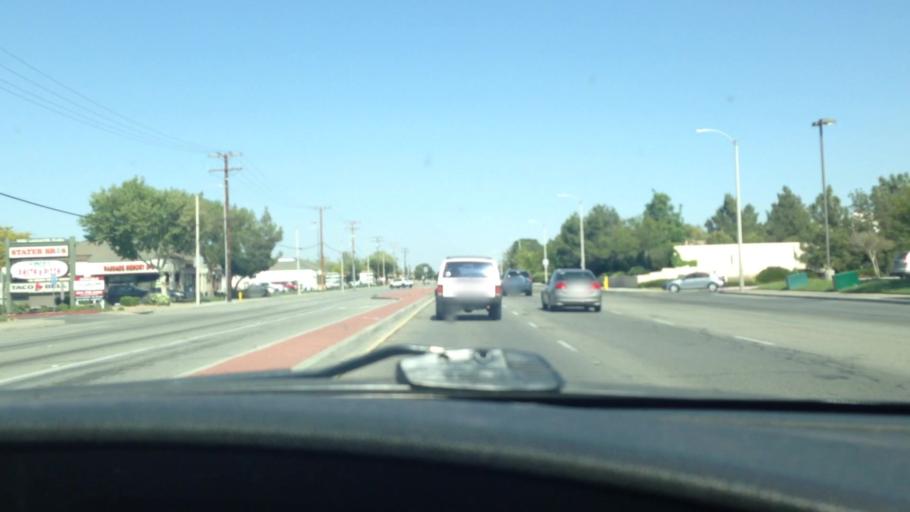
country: US
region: California
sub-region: Los Angeles County
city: Quartz Hill
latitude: 34.6603
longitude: -118.1831
